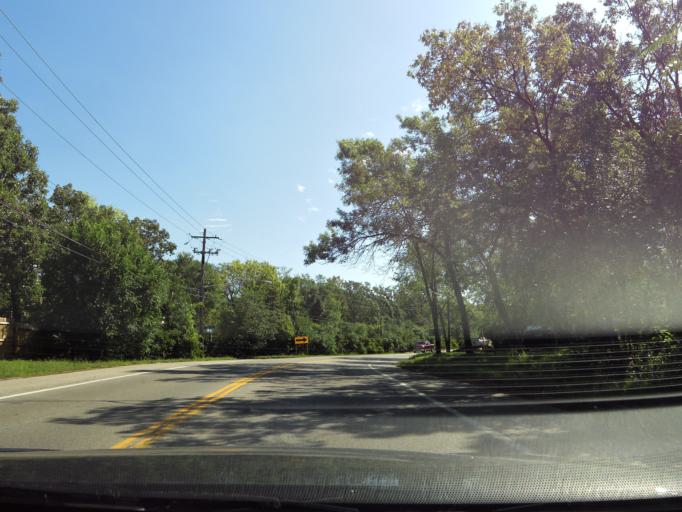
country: US
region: Minnesota
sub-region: Hennepin County
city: Hopkins
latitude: 44.9418
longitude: -93.4866
